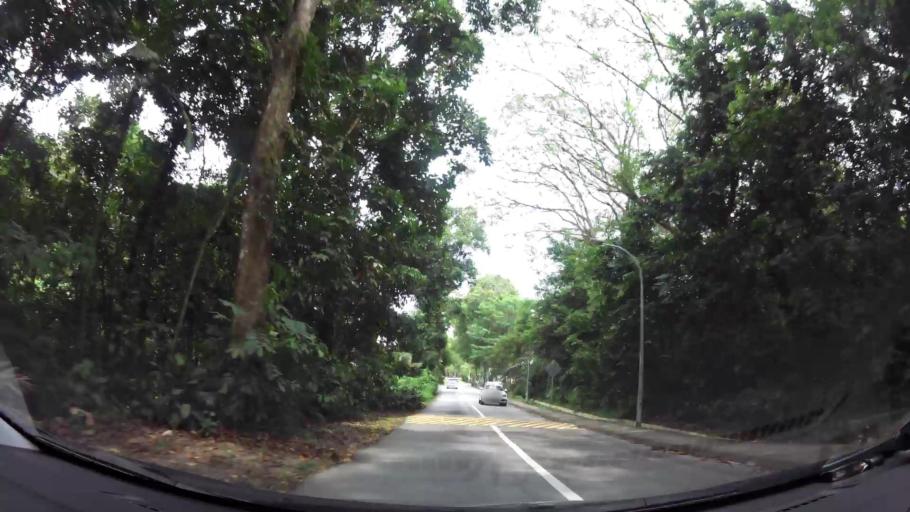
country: SG
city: Singapore
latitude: 1.3219
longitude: 103.7822
